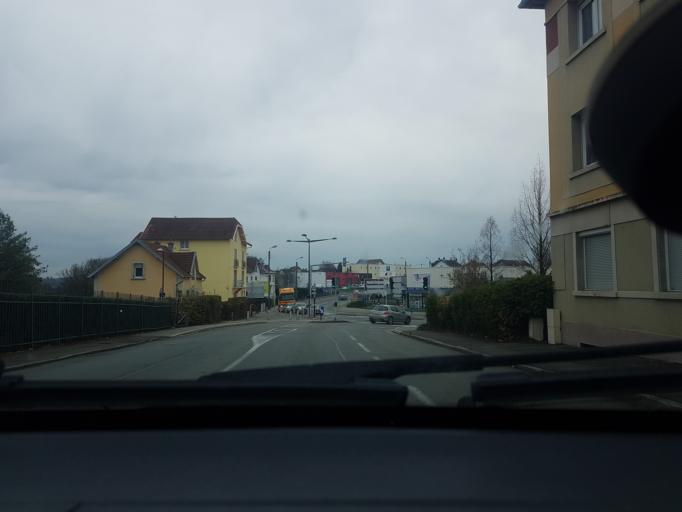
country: FR
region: Franche-Comte
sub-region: Territoire de Belfort
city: Bavilliers
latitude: 47.6281
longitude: 6.8455
